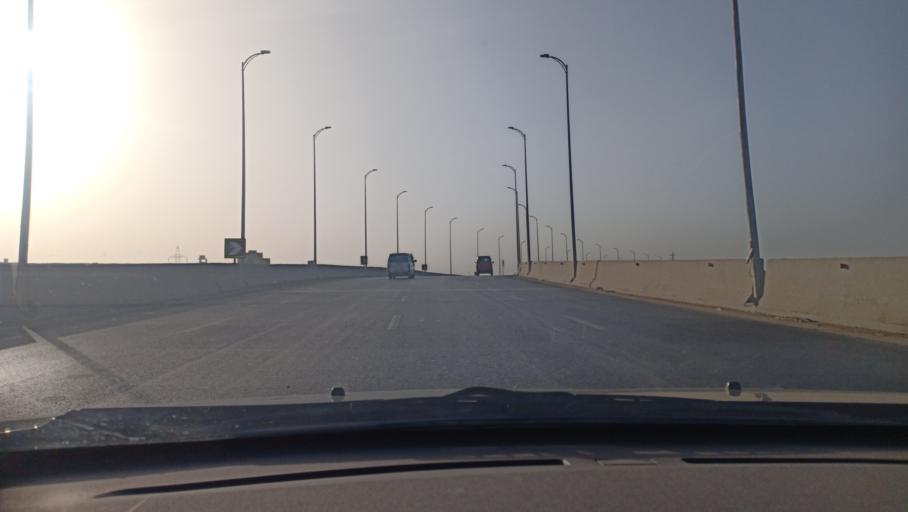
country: EG
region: Muhafazat al Qalyubiyah
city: Qalyub
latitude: 30.1471
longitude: 31.2571
